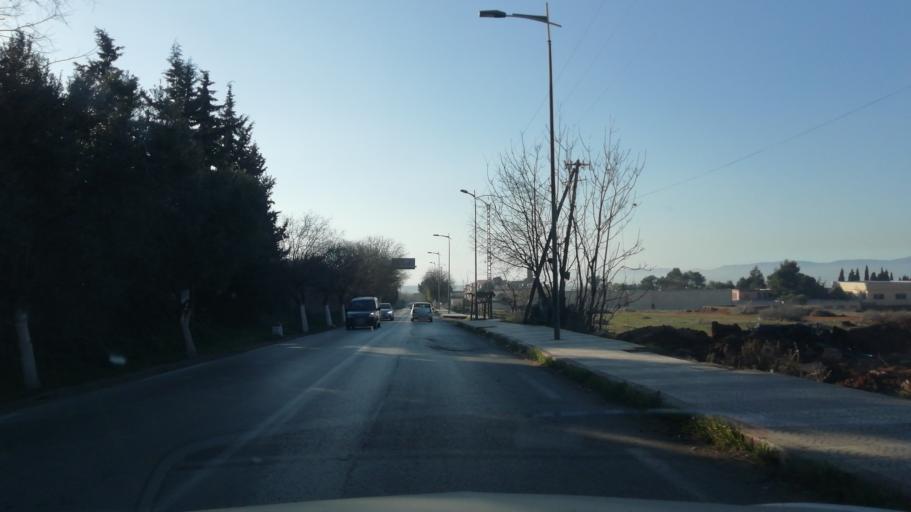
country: DZ
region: Tlemcen
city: Beni Mester
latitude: 34.8663
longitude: -1.4218
